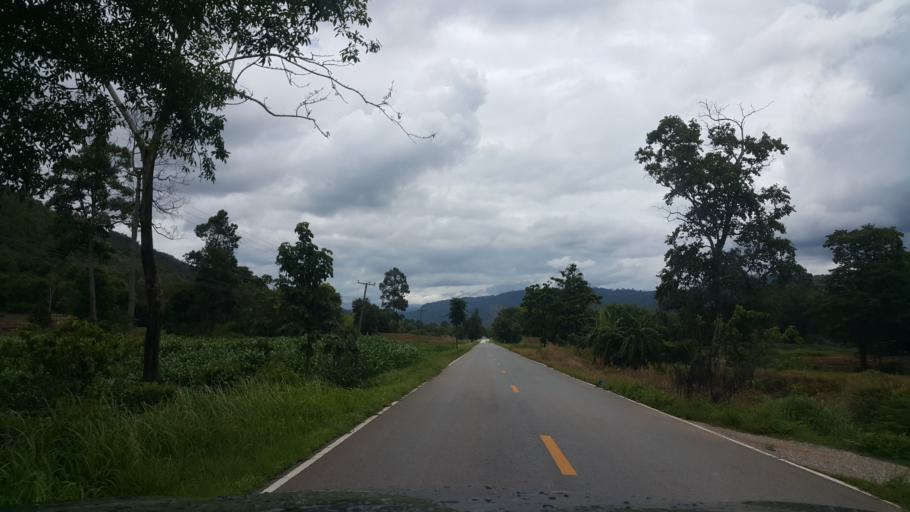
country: TH
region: Phitsanulok
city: Chat Trakan
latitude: 17.3197
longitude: 100.6830
